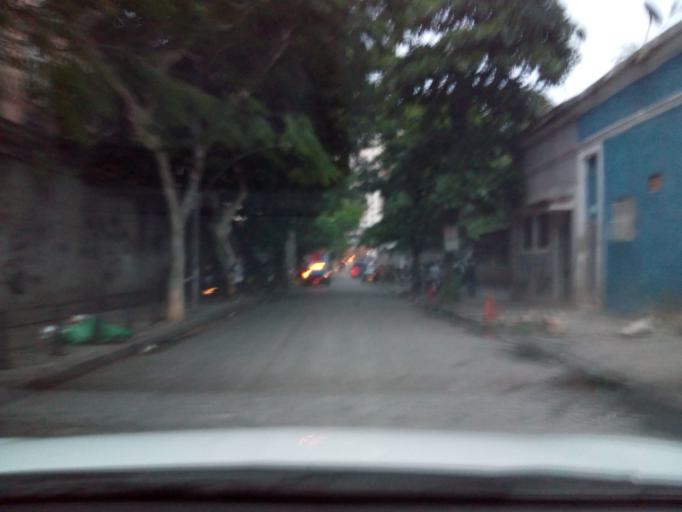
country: BR
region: Rio de Janeiro
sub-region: Rio De Janeiro
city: Rio de Janeiro
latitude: -22.9062
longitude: -43.1912
